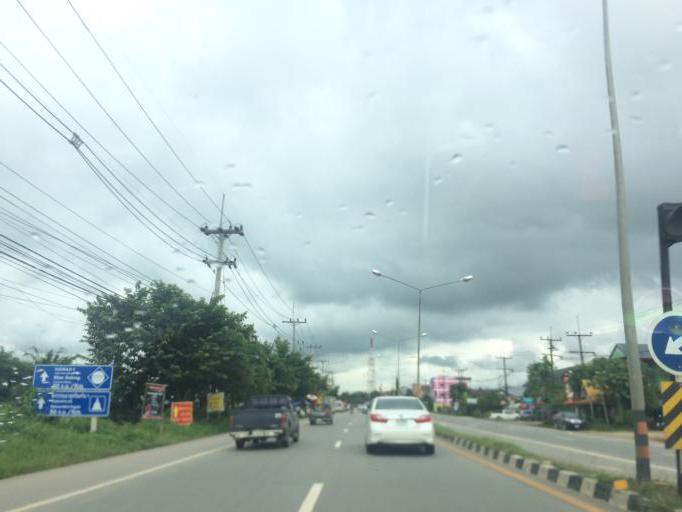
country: TH
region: Chiang Rai
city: Mae Chan
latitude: 20.0401
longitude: 99.8758
